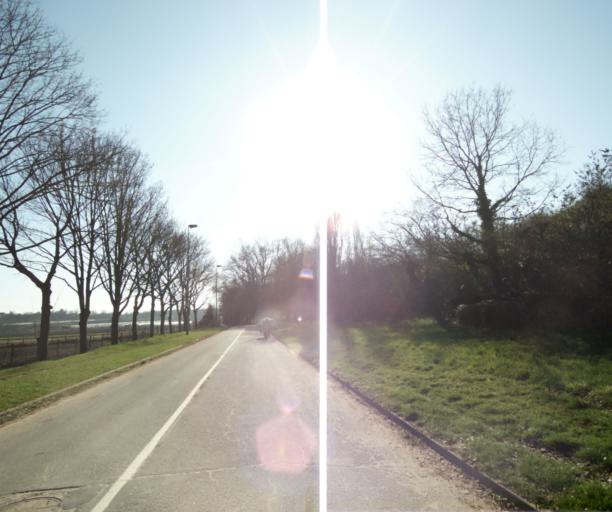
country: FR
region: Ile-de-France
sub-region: Departement du Val-d'Oise
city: Cergy
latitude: 49.0256
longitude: 2.0859
